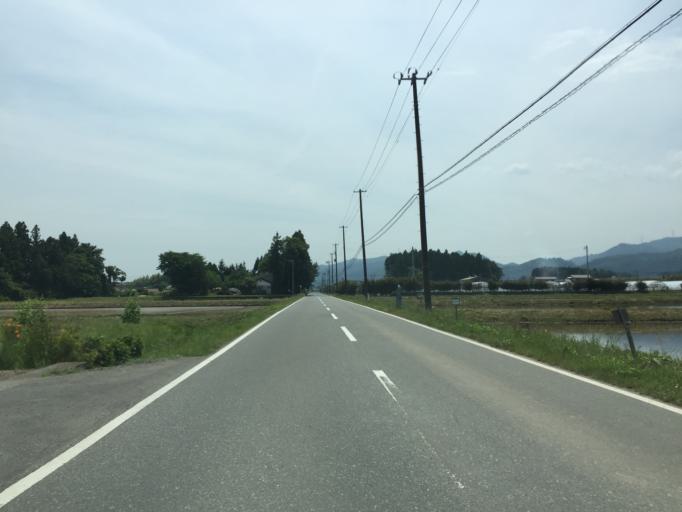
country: JP
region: Fukushima
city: Namie
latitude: 37.6175
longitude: 140.9316
